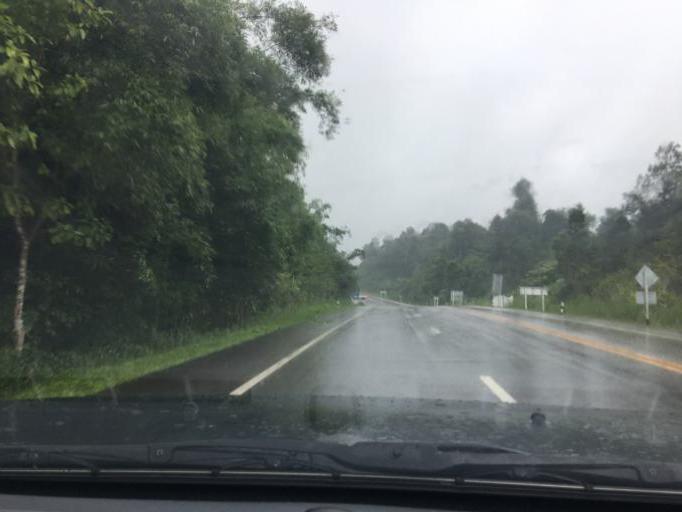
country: TH
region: Lampang
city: Wang Nuea
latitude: 19.0731
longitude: 99.3908
